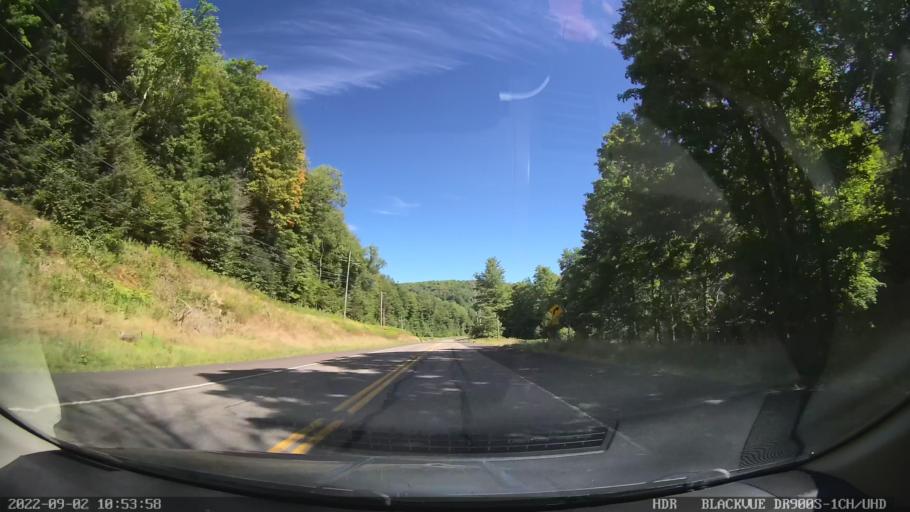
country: US
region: Pennsylvania
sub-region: Tioga County
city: Blossburg
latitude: 41.6533
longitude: -77.0949
